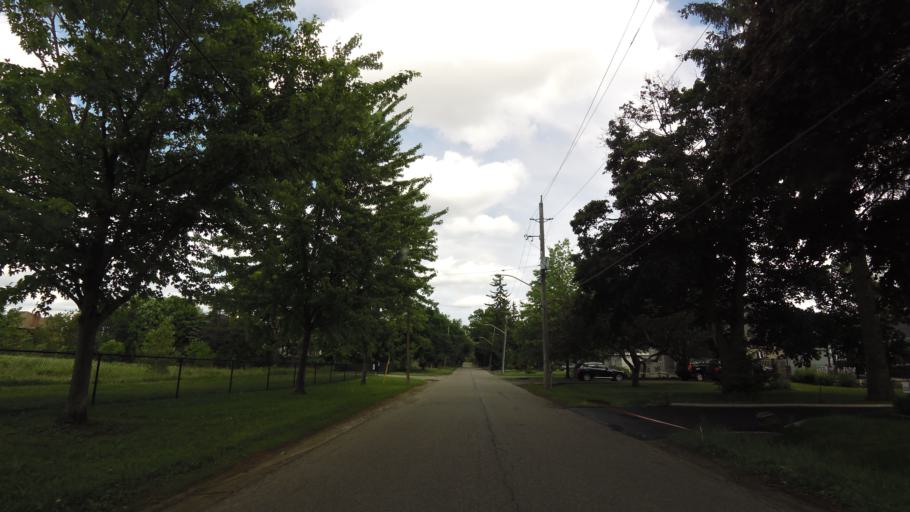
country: CA
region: Ontario
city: Mississauga
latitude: 43.5344
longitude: -79.6428
